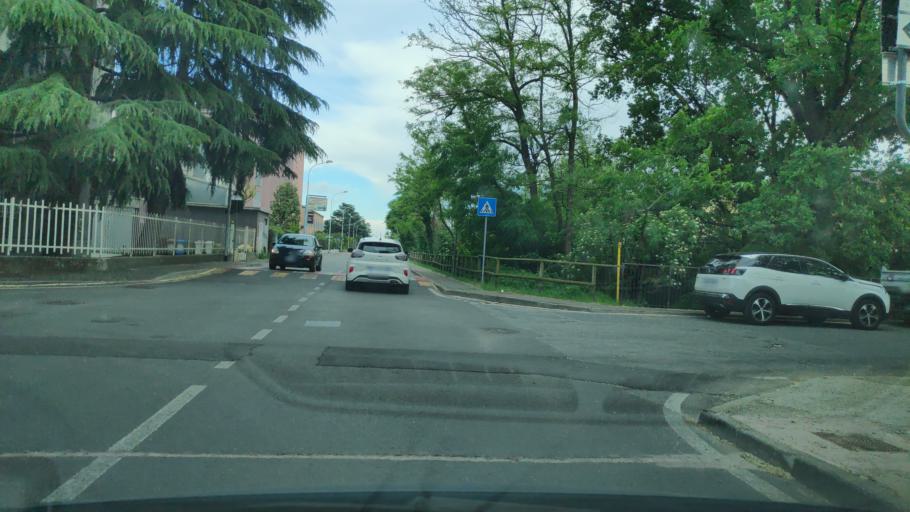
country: IT
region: Lombardy
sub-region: Citta metropolitana di Milano
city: Fizzonasco
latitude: 45.3733
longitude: 9.1811
